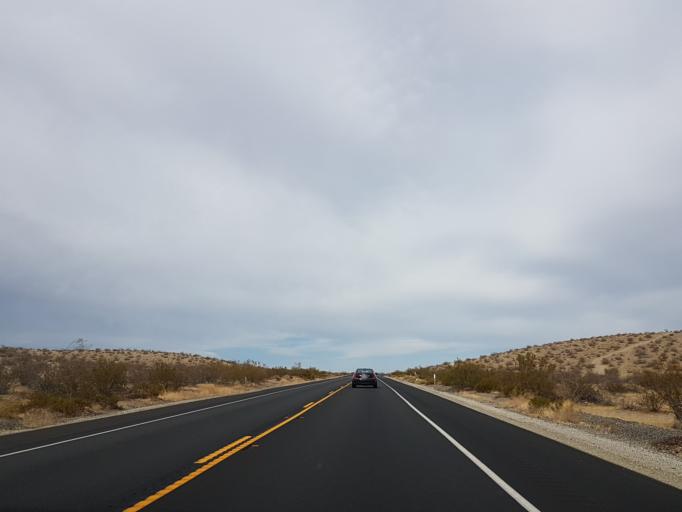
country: US
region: California
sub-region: Kern County
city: Ridgecrest
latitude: 35.4577
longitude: -117.6548
